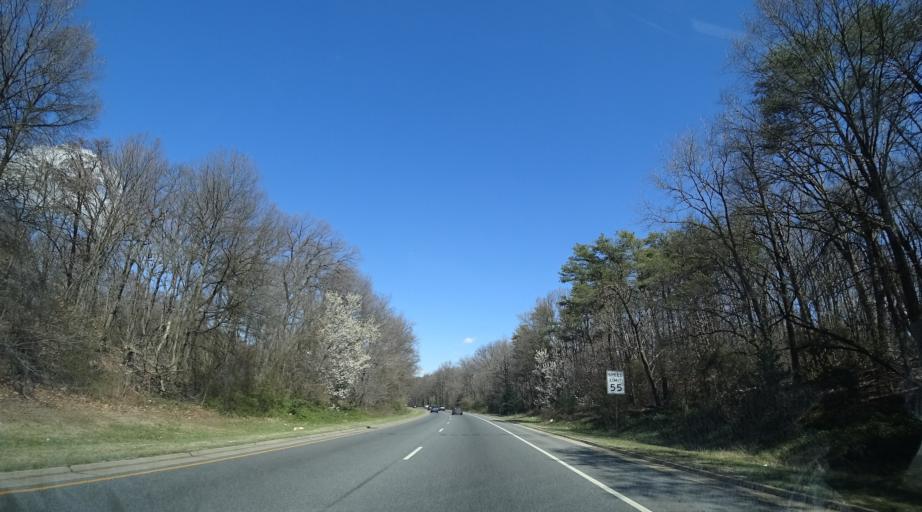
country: US
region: Maryland
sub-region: Prince George's County
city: Landover
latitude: 38.9443
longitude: -76.9094
